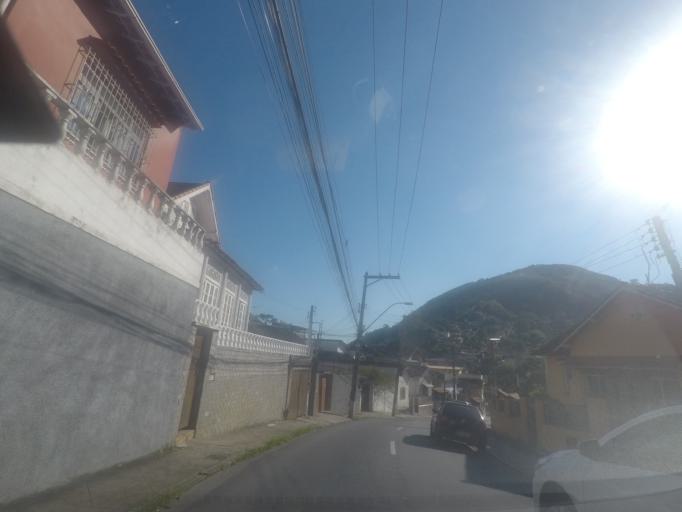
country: BR
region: Rio de Janeiro
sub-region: Petropolis
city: Petropolis
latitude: -22.5153
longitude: -43.1681
